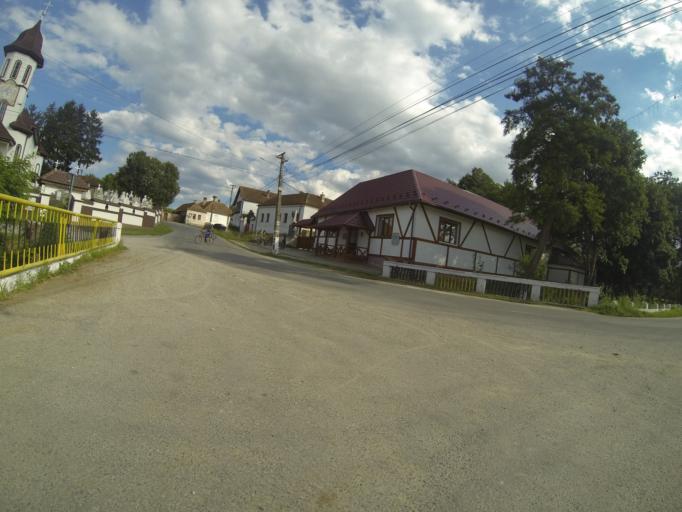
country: RO
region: Brasov
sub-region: Comuna Sinca Veche
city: Sinca Veche
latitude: 45.7412
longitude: 25.0962
